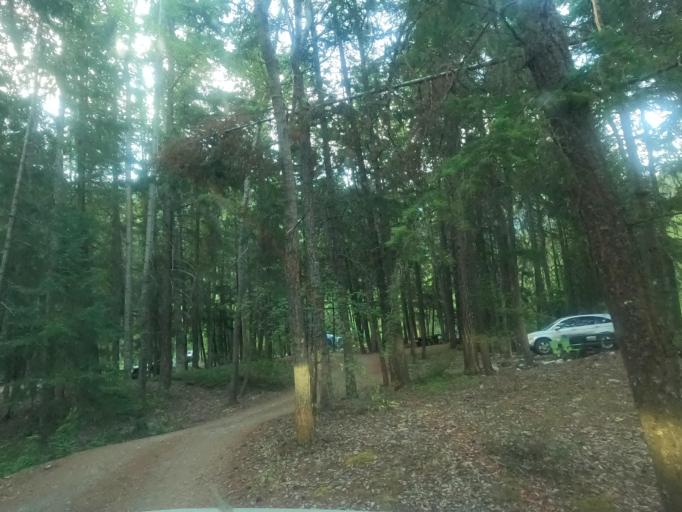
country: CA
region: British Columbia
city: Lillooet
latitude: 50.5826
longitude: -122.0922
